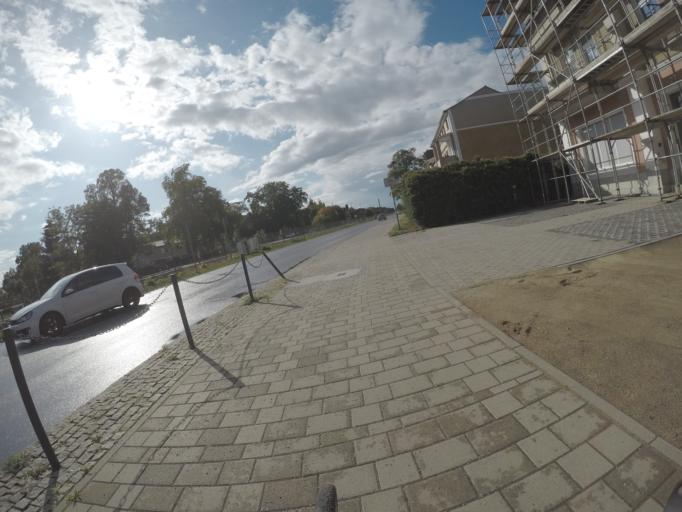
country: DE
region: Brandenburg
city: Petershagen
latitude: 52.5319
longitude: 13.8438
